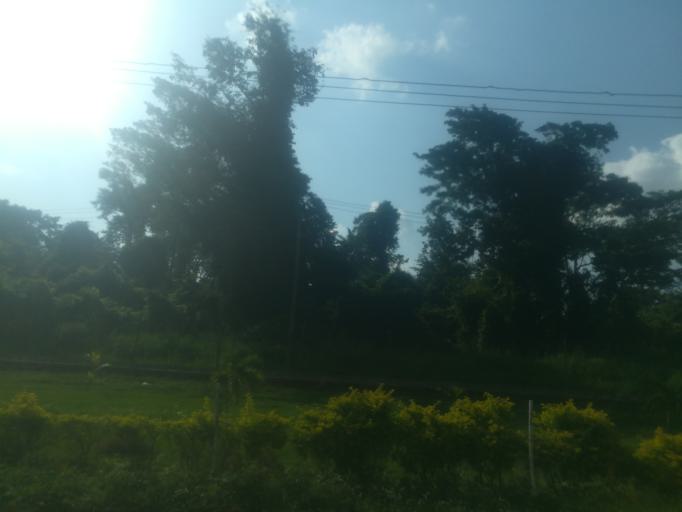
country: NG
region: Oyo
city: Moniya
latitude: 7.4927
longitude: 3.9142
